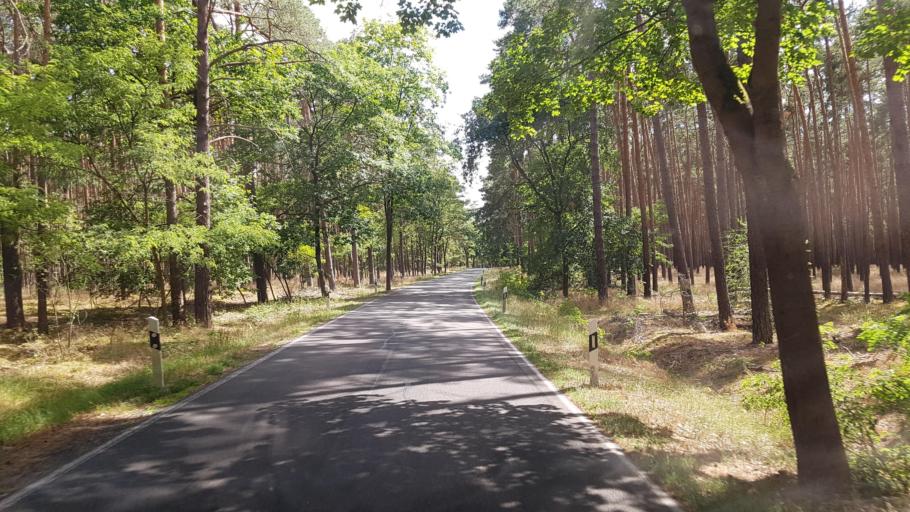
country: DE
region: Brandenburg
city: Luckenwalde
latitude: 52.1329
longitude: 13.1910
